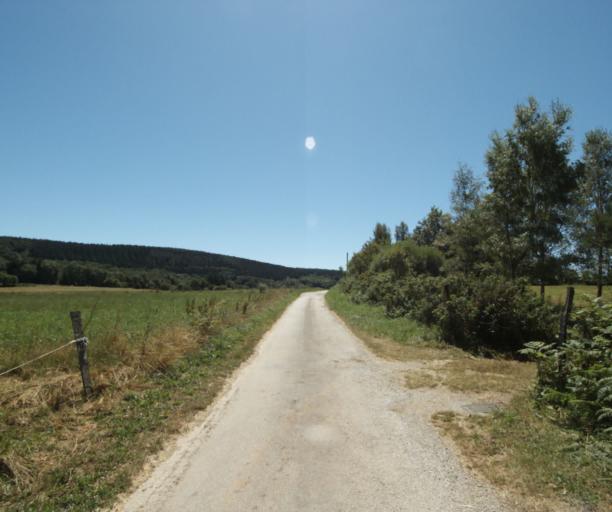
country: FR
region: Midi-Pyrenees
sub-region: Departement du Tarn
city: Dourgne
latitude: 43.4284
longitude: 2.1663
